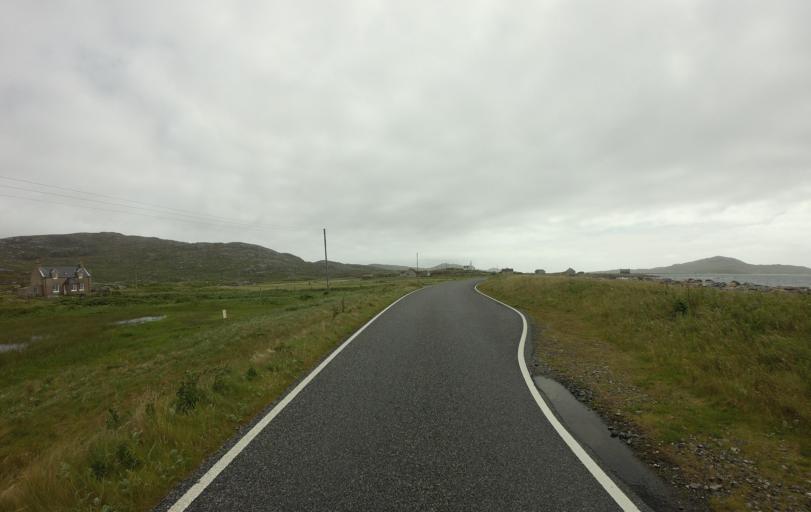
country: GB
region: Scotland
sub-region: Eilean Siar
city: Isle of South Uist
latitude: 57.1037
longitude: -7.3472
